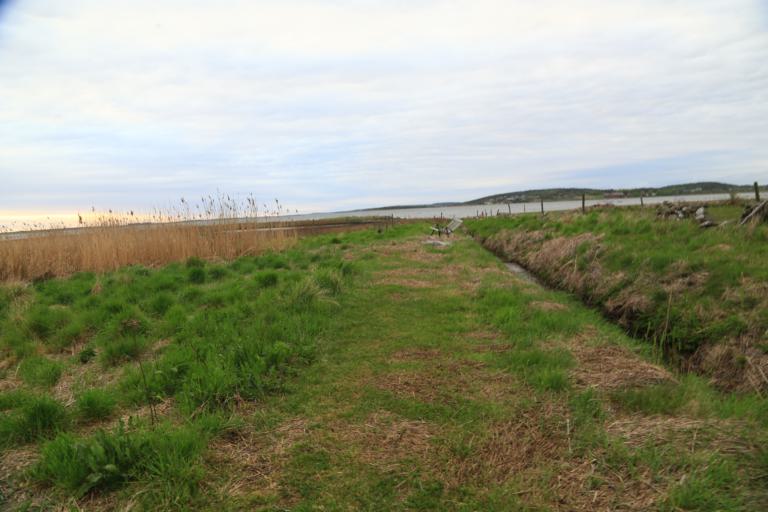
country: SE
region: Halland
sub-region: Varbergs Kommun
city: Varberg
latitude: 57.1536
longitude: 12.2272
